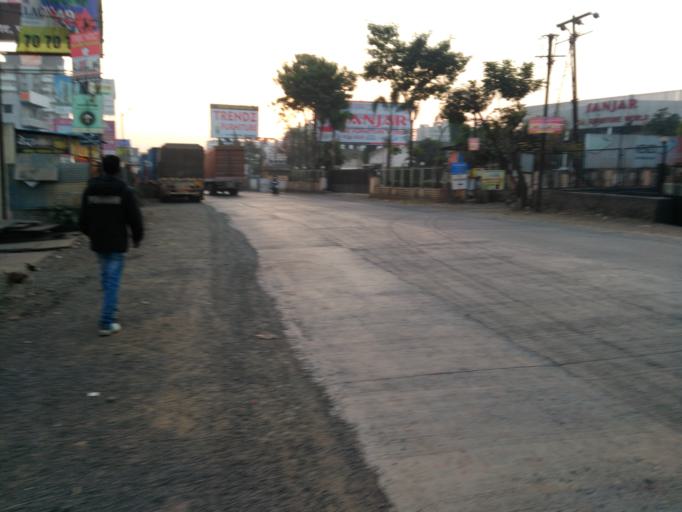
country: IN
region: Maharashtra
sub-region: Pune Division
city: Pune
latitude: 18.4504
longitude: 73.9006
